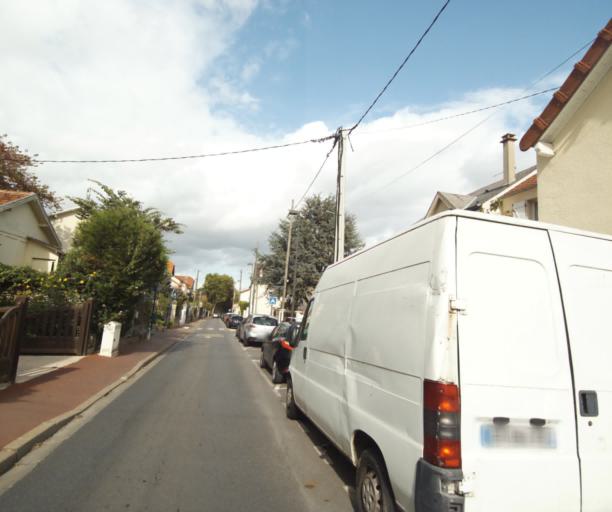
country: FR
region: Ile-de-France
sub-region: Departement des Hauts-de-Seine
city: Issy-les-Moulineaux
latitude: 48.8099
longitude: 2.2791
